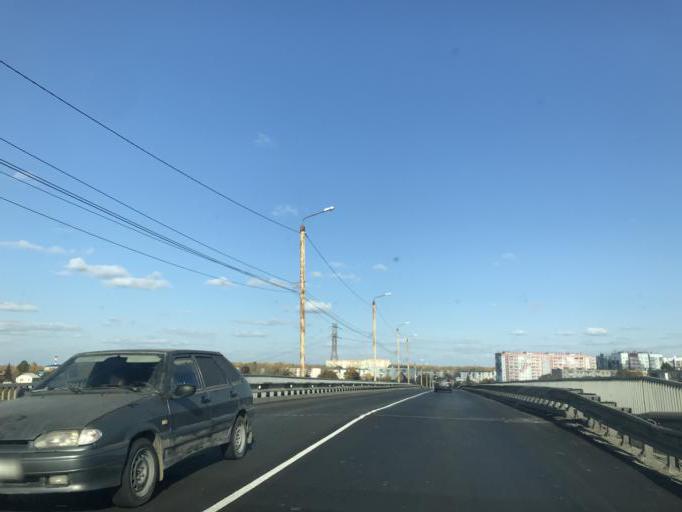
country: RU
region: Chelyabinsk
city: Roshchino
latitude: 55.2331
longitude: 61.2924
